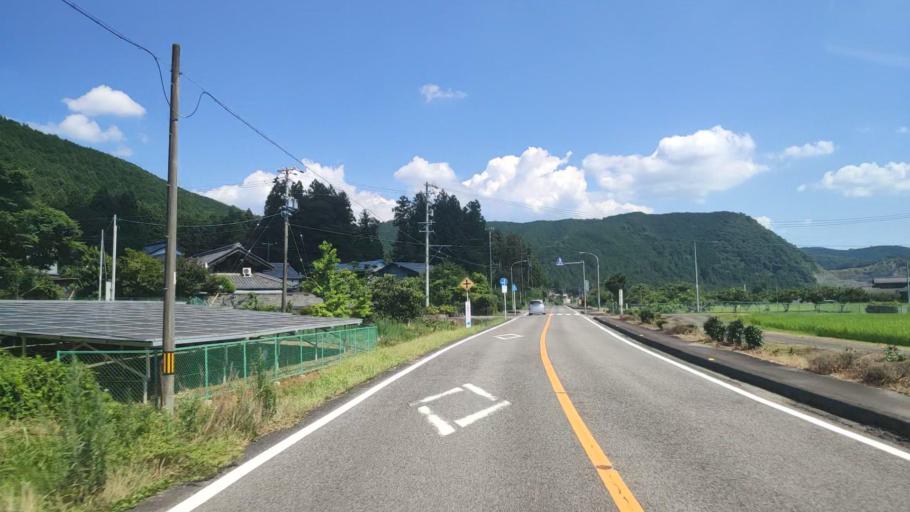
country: JP
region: Gifu
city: Godo
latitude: 35.5392
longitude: 136.6470
